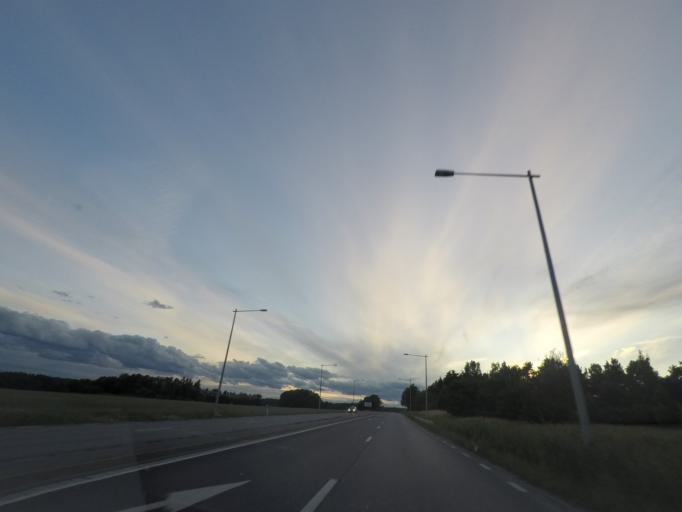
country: SE
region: Stockholm
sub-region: Sigtuna Kommun
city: Marsta
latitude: 59.6269
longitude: 17.8210
